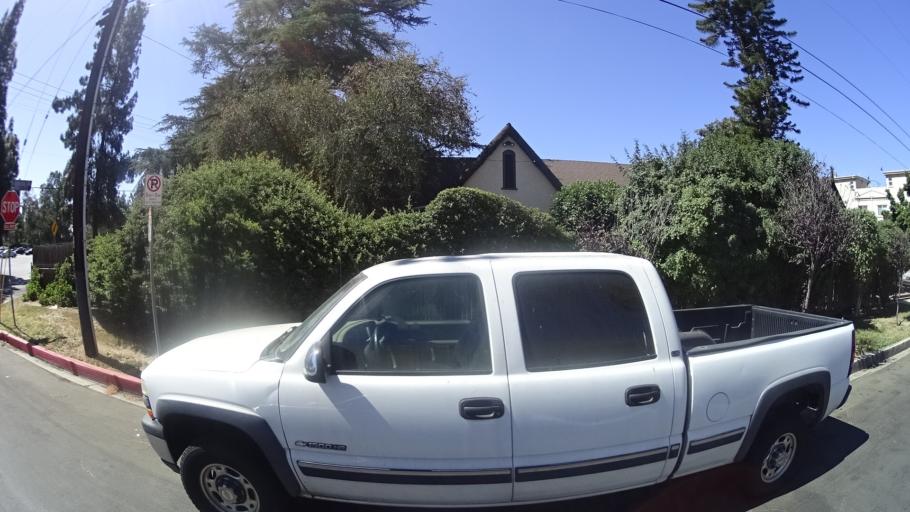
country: US
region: California
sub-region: Los Angeles County
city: Van Nuys
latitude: 34.1903
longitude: -118.4905
